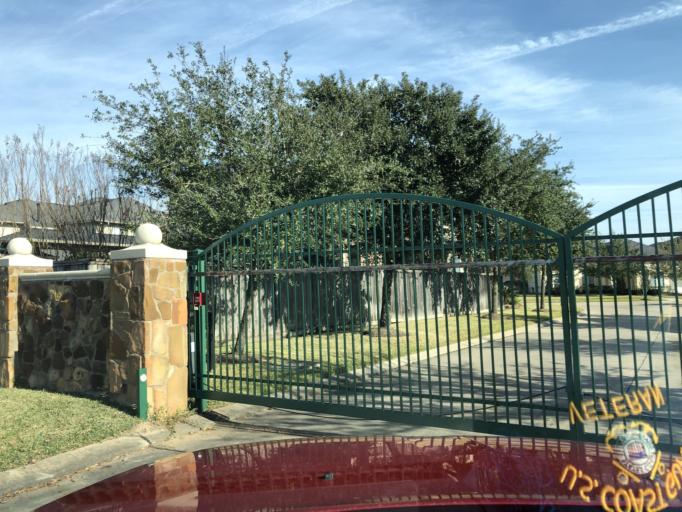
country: US
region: Texas
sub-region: Harris County
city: Tomball
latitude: 30.0385
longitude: -95.5520
